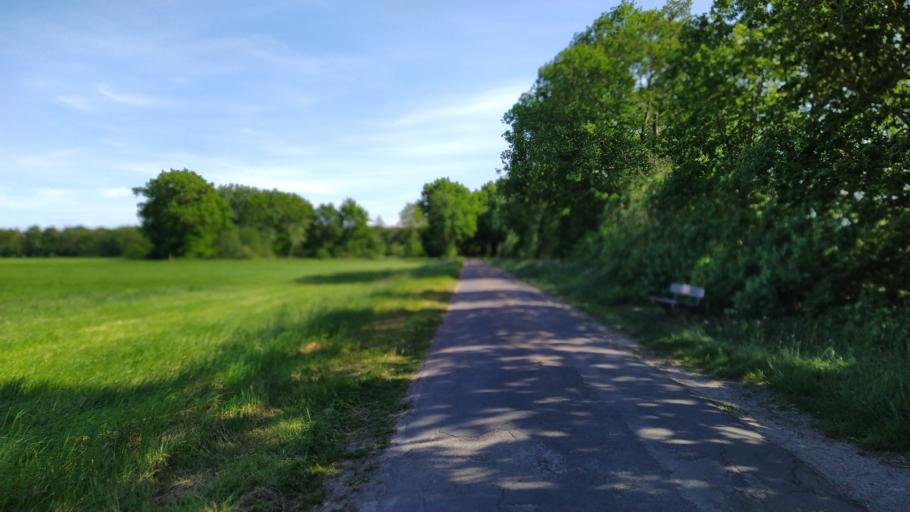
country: DE
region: Lower Saxony
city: Ahlerstedt
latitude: 53.4290
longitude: 9.4707
